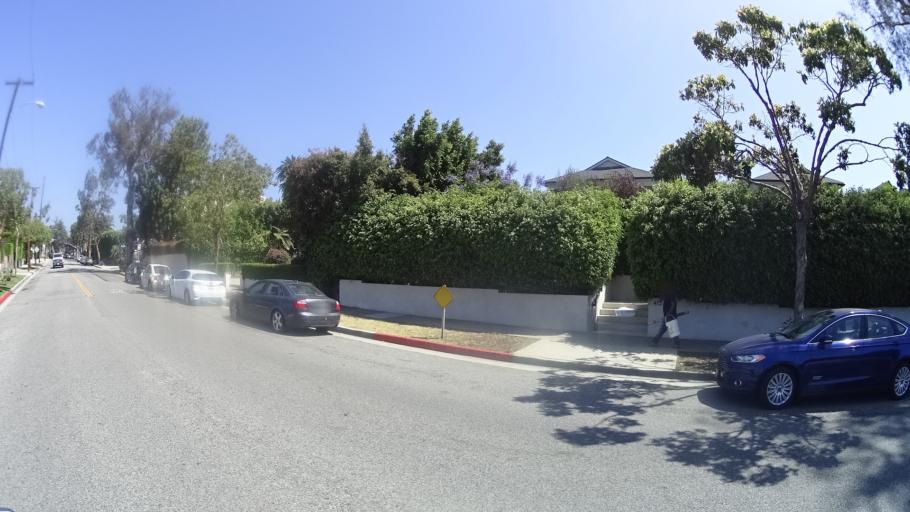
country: US
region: California
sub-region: Los Angeles County
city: Santa Monica
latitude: 34.0308
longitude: -118.5066
